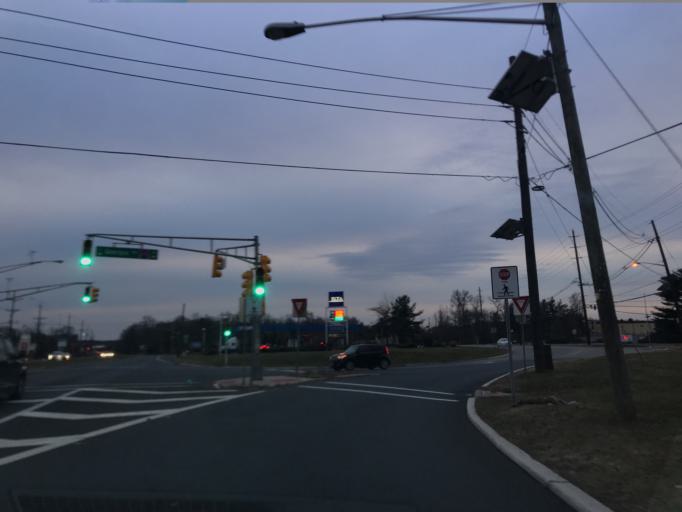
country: US
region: New Jersey
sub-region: Middlesex County
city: Dayton
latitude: 40.4117
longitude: -74.5060
